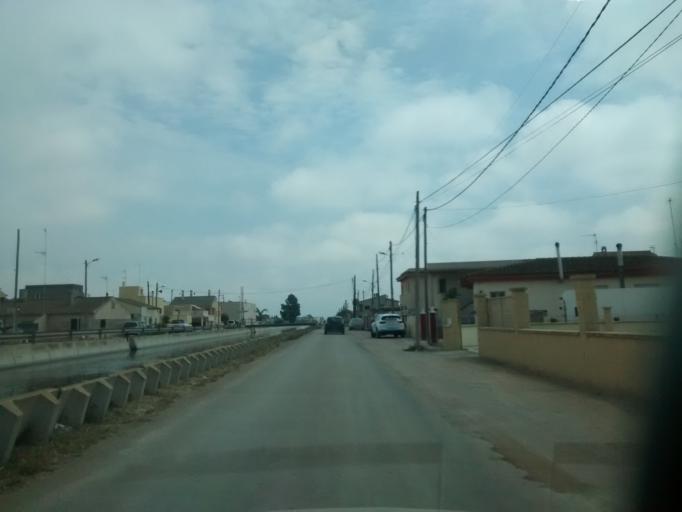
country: ES
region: Catalonia
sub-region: Provincia de Tarragona
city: Deltebre
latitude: 40.7035
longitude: 0.7195
